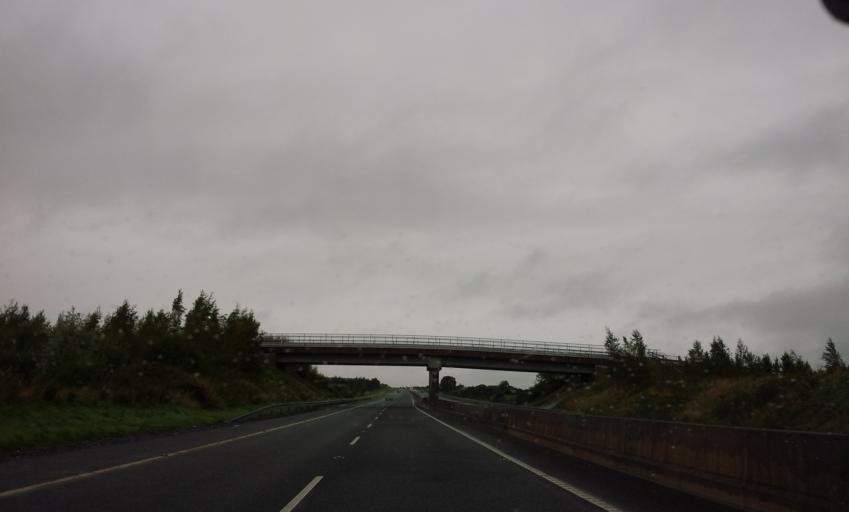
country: IE
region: Munster
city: Cashel
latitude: 52.4553
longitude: -7.9080
